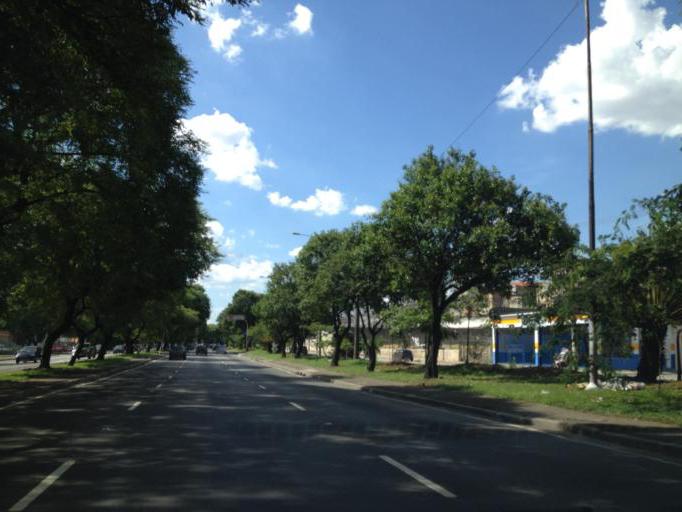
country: BR
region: Sao Paulo
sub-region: Sao Paulo
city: Sao Paulo
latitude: -23.5520
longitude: -46.5774
